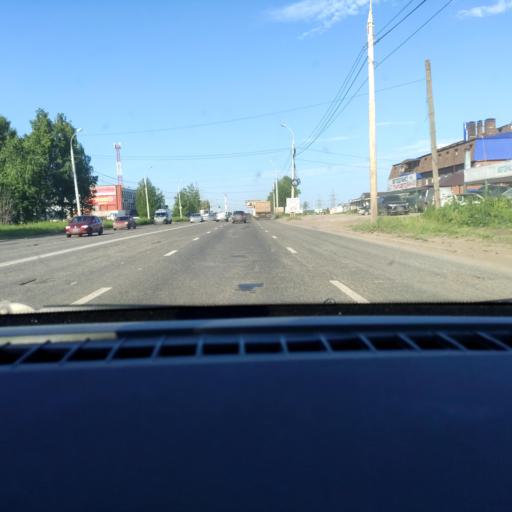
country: RU
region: Udmurtiya
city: Khokhryaki
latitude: 56.9009
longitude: 53.3185
